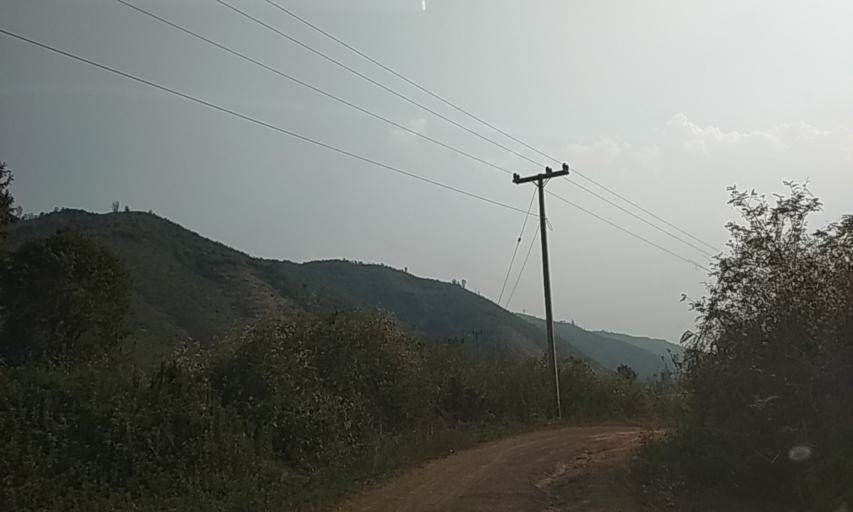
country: LA
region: Louangphabang
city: Louangphabang
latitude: 20.0316
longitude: 101.7898
